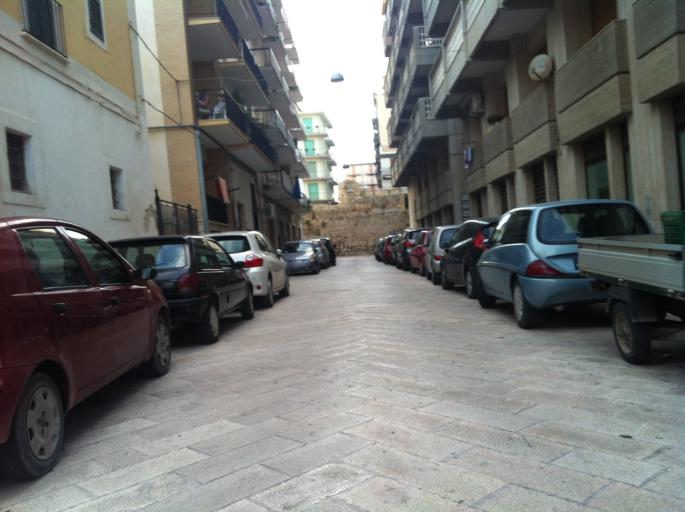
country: IT
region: Apulia
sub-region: Provincia di Foggia
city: Manfredonia
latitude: 41.6307
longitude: 15.9185
